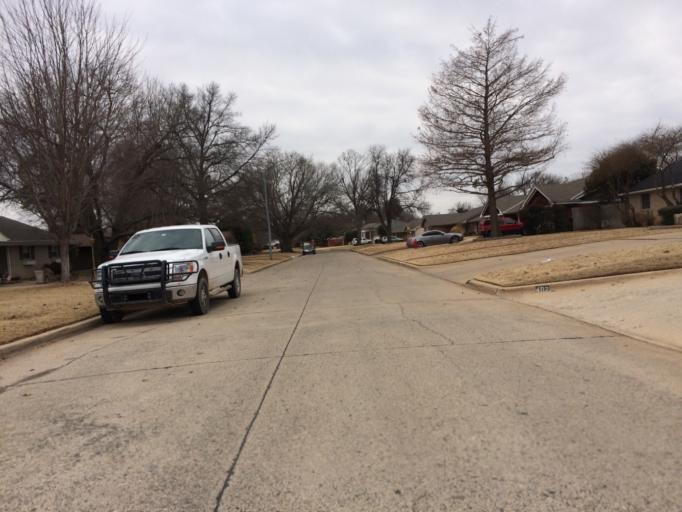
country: US
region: Oklahoma
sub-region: Cleveland County
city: Norman
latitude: 35.2231
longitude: -97.4717
